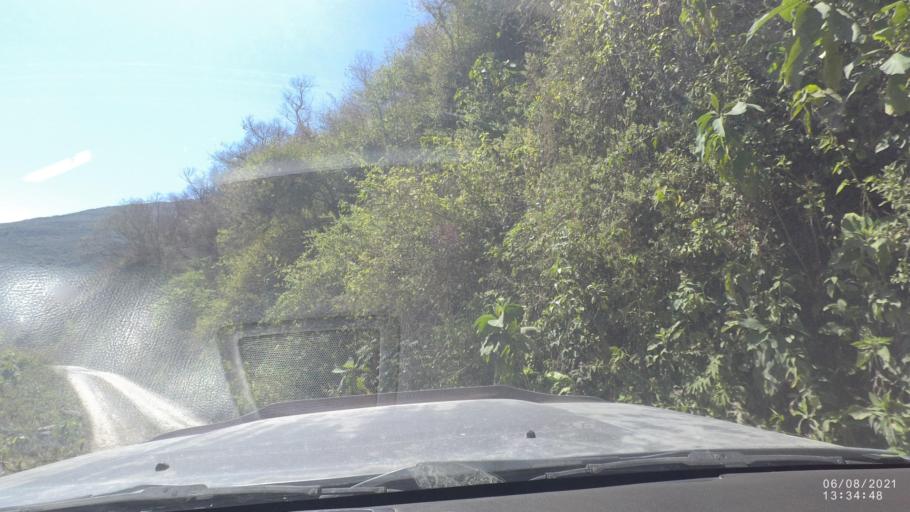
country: BO
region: La Paz
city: Quime
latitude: -16.6942
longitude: -66.7220
